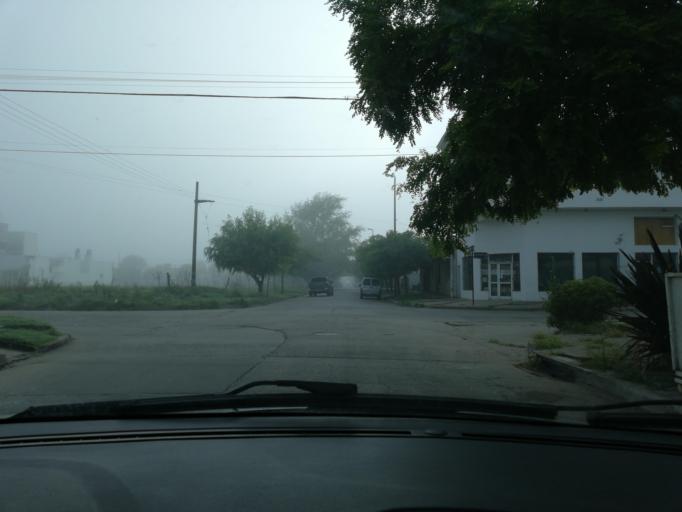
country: AR
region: Buenos Aires
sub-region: Partido de Balcarce
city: Balcarce
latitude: -37.8435
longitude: -58.2498
